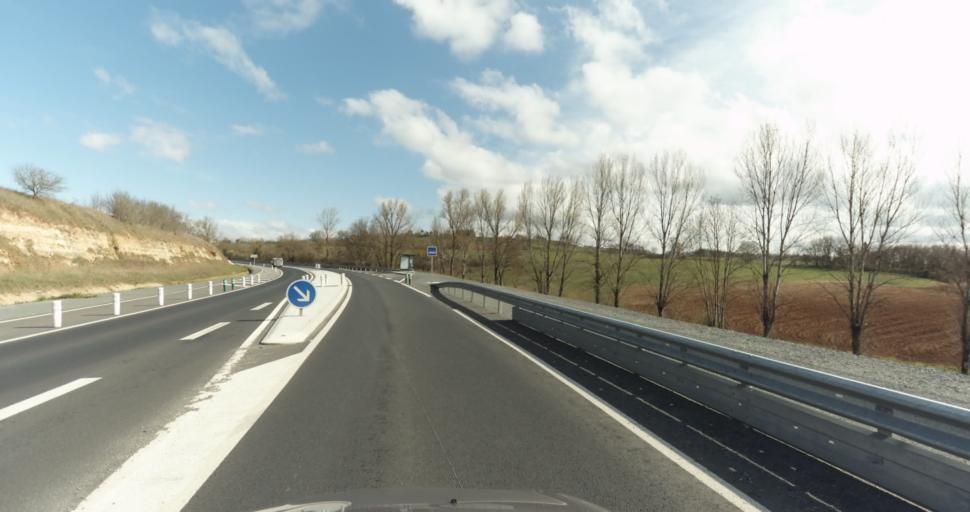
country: FR
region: Midi-Pyrenees
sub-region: Departement du Tarn
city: Frejairolles
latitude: 43.8570
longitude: 2.1893
